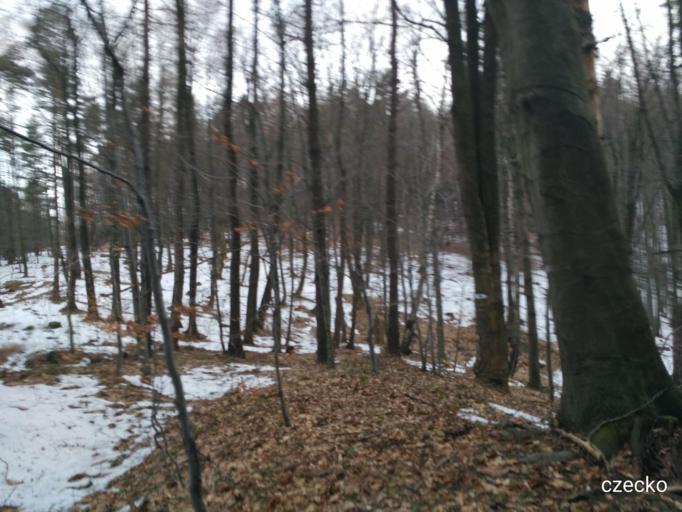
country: PL
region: Subcarpathian Voivodeship
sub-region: Powiat krosnienski
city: Korczyna
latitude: 49.7519
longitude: 21.8260
